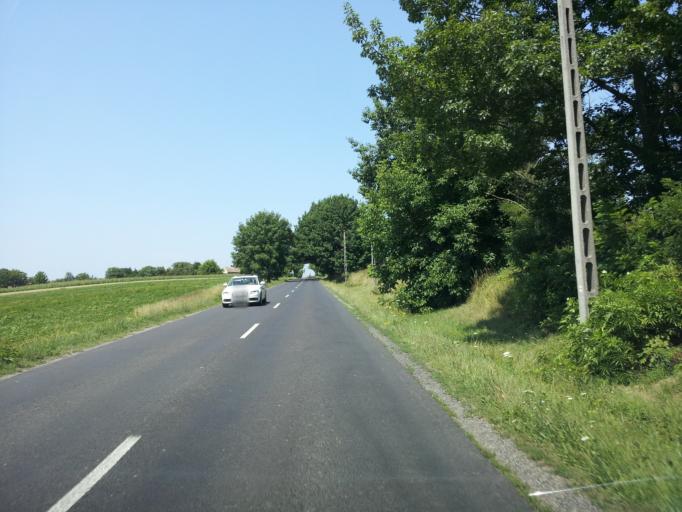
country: HU
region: Zala
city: Zalaegerszeg
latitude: 46.8603
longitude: 16.8130
